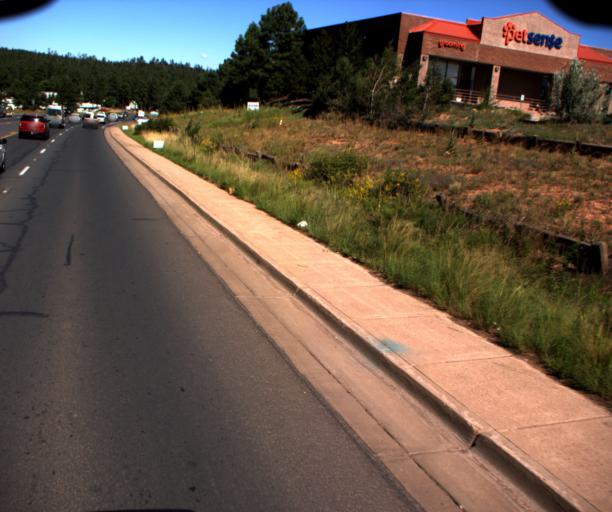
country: US
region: Arizona
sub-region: Navajo County
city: Show Low
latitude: 34.2108
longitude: -110.0254
